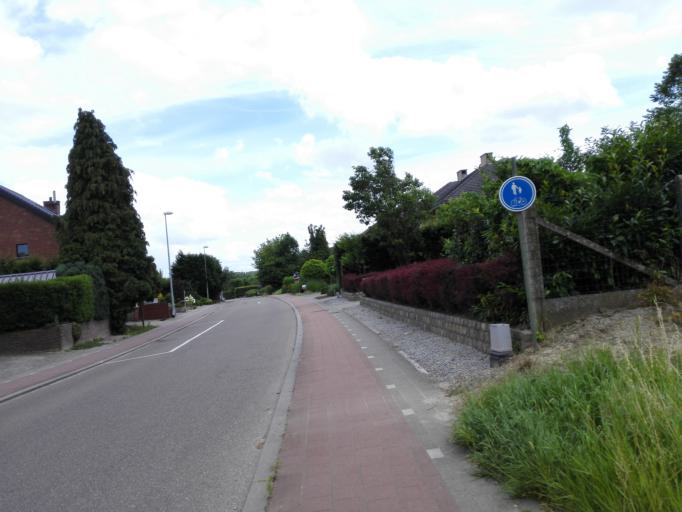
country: BE
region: Flanders
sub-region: Provincie Vlaams-Brabant
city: Bierbeek
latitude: 50.8608
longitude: 4.7559
